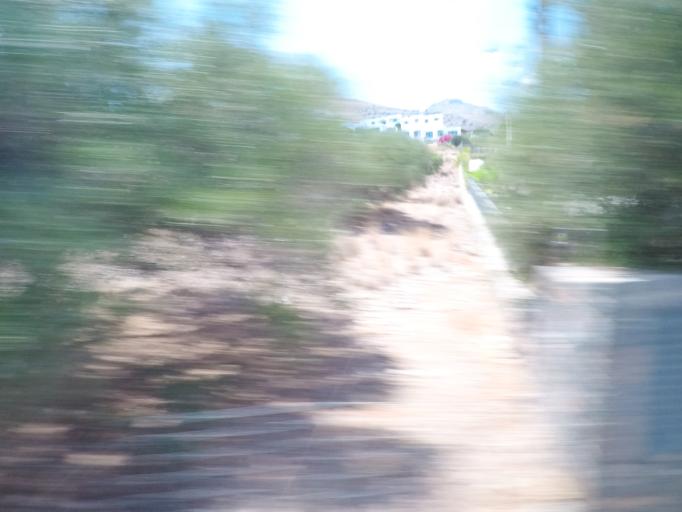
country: GR
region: Crete
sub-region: Nomos Lasithiou
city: Skhisma
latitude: 35.2431
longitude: 25.7296
